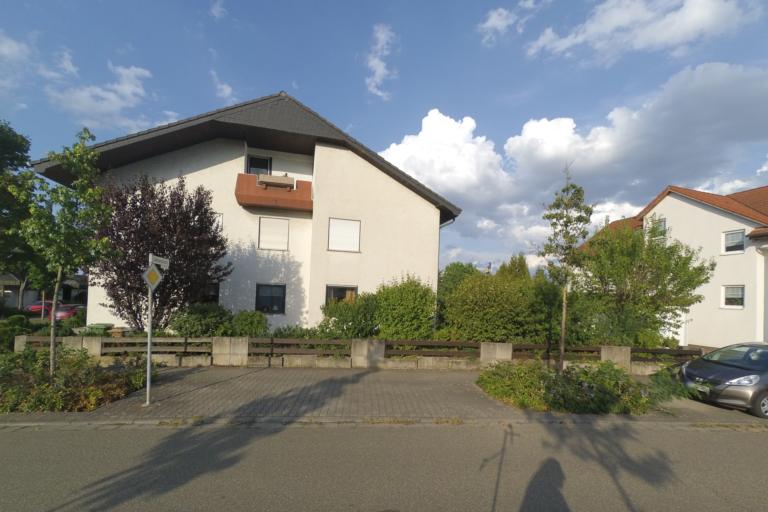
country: DE
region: Hesse
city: Lampertheim
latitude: 49.5837
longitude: 8.4884
